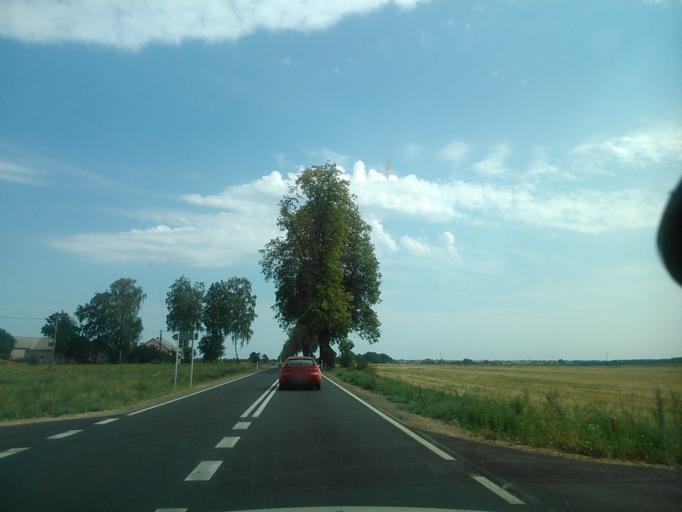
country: PL
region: Warmian-Masurian Voivodeship
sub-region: Powiat dzialdowski
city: Dzialdowo
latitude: 53.2348
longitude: 20.1107
